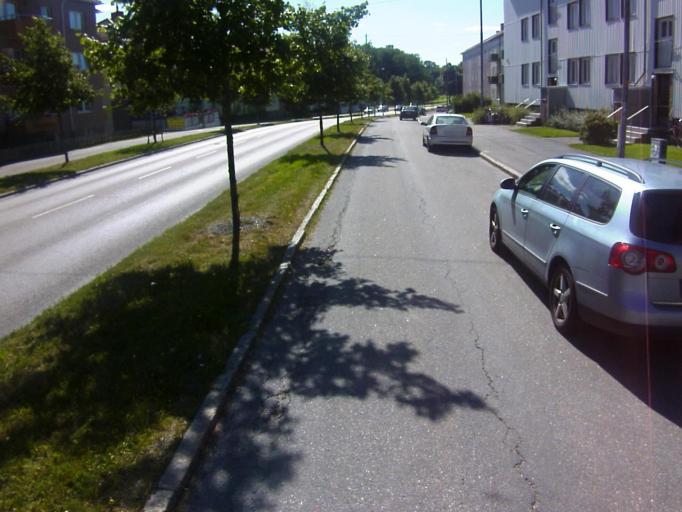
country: SE
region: Soedermanland
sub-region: Eskilstuna Kommun
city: Eskilstuna
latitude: 59.3709
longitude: 16.5330
